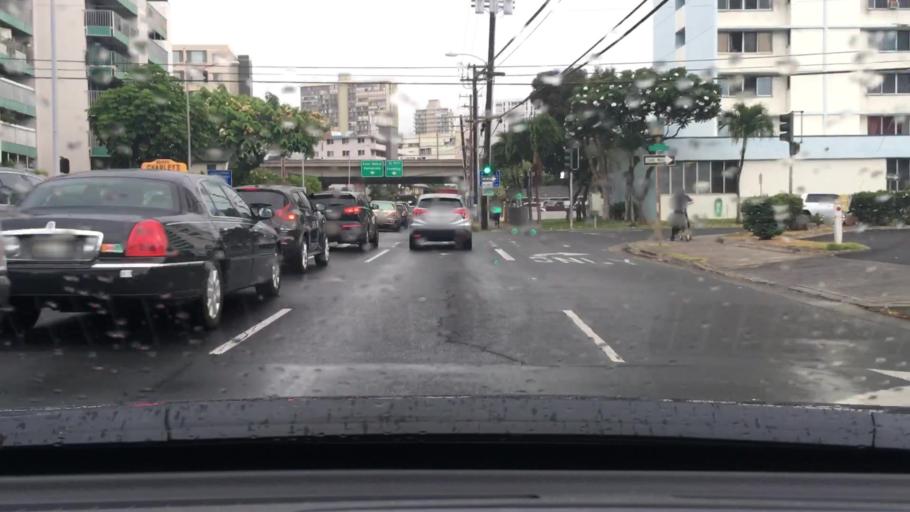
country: US
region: Hawaii
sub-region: Honolulu County
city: Honolulu
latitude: 21.3021
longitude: -157.8429
